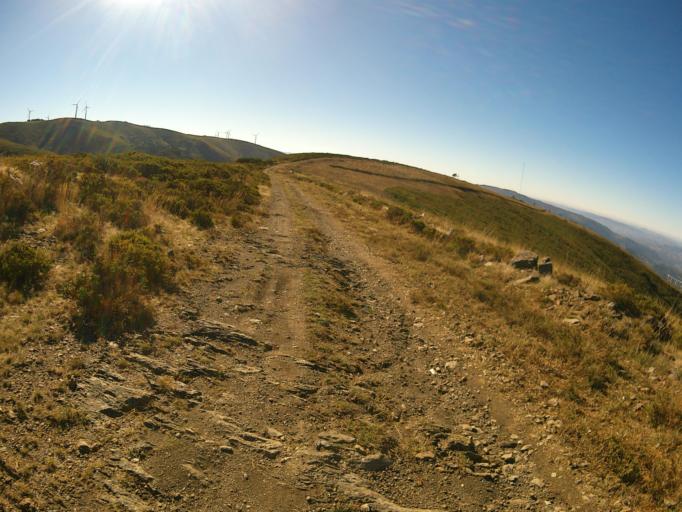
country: PT
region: Vila Real
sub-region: Mesao Frio
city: Mesao Frio
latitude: 41.2518
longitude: -7.9133
